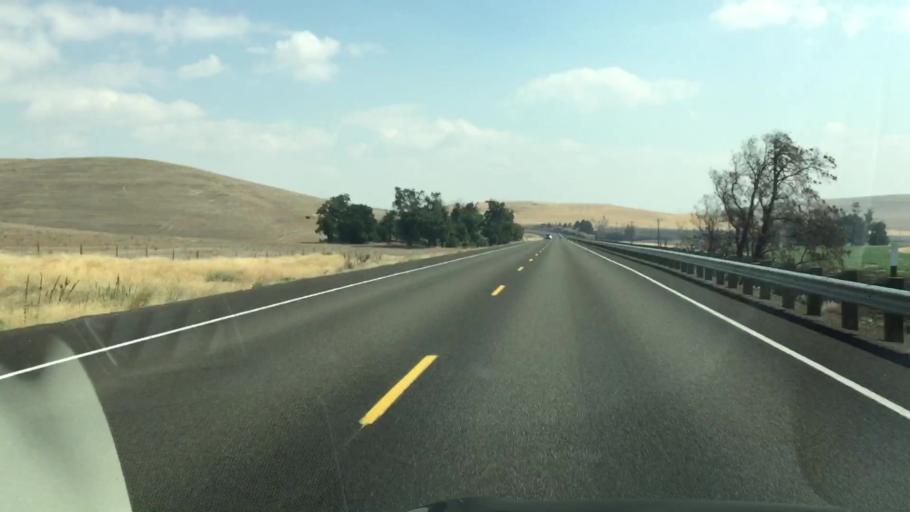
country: US
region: Oregon
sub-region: Wasco County
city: The Dalles
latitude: 45.4895
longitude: -121.1026
